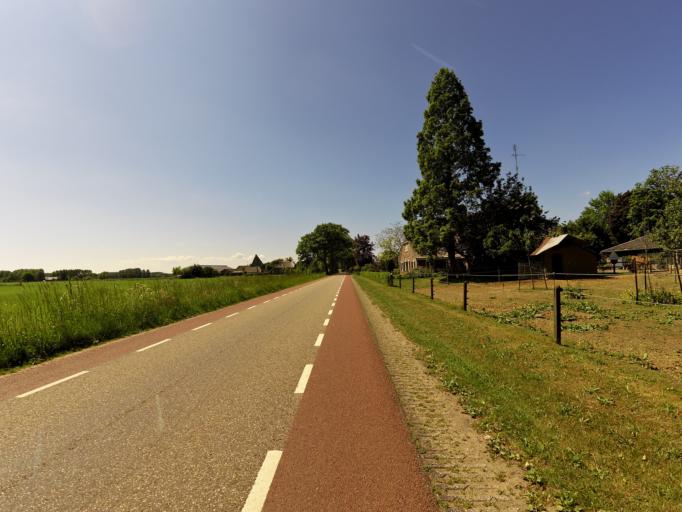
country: NL
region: Gelderland
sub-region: Gemeente Bronckhorst
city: Hengelo
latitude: 52.0704
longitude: 6.2926
